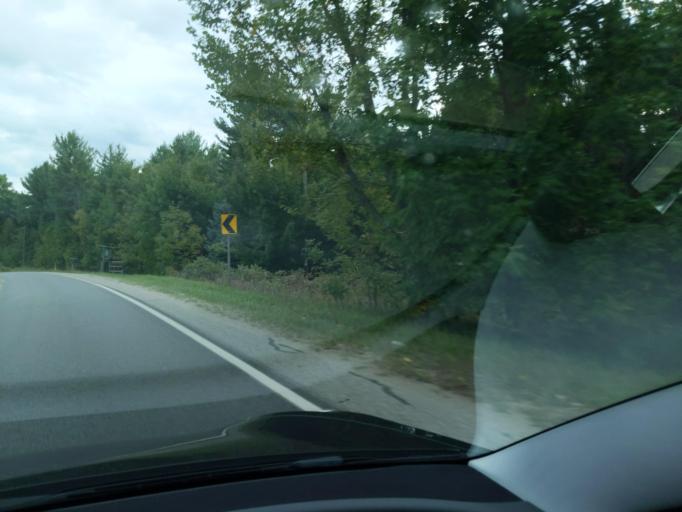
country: US
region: Michigan
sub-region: Kalkaska County
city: Rapid City
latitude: 44.7908
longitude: -85.2776
